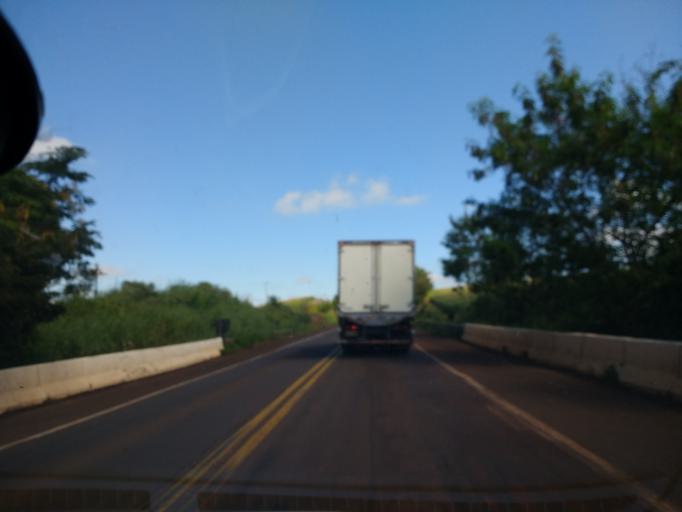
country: BR
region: Parana
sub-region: Terra Boa
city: Terra Boa
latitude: -23.5981
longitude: -52.3927
